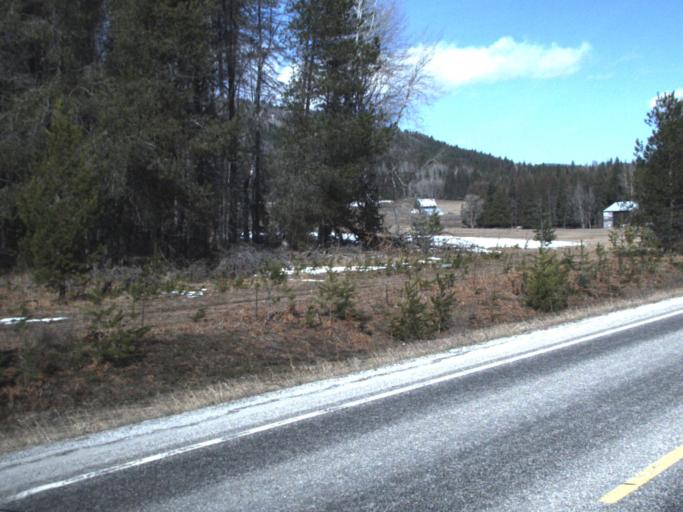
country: CA
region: British Columbia
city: Fruitvale
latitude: 48.6606
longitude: -117.3906
